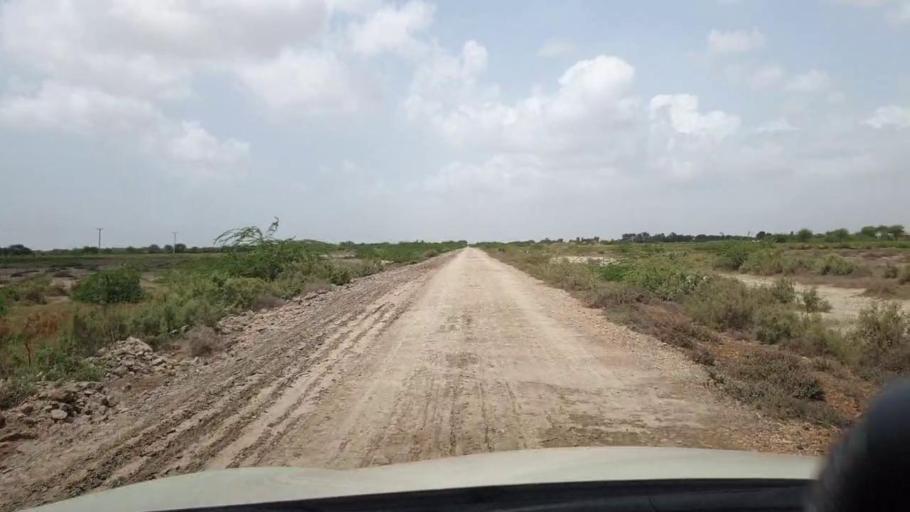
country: PK
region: Sindh
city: Kadhan
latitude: 24.3731
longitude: 68.8561
